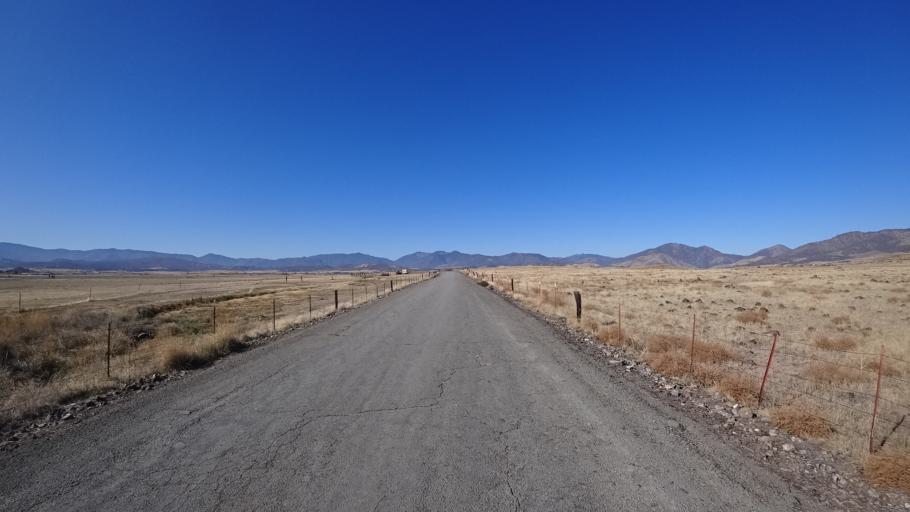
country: US
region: California
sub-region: Siskiyou County
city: Montague
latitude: 41.7422
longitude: -122.5318
